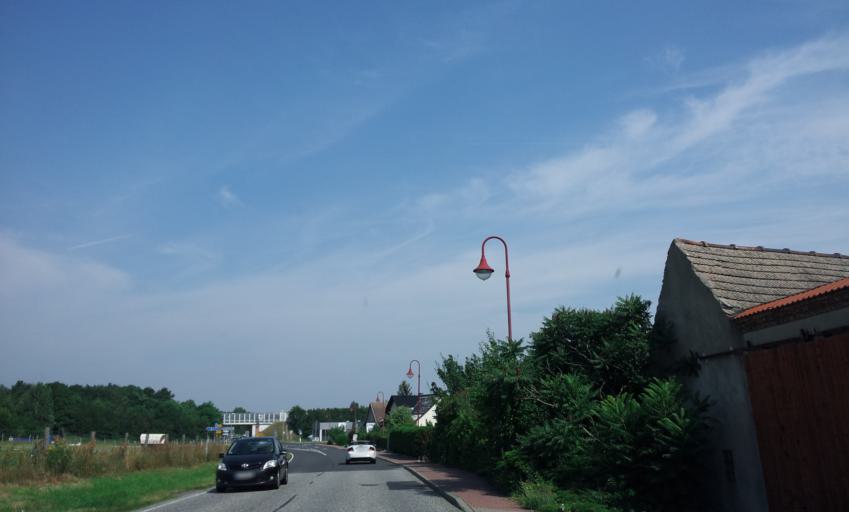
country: DE
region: Brandenburg
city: Linthe
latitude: 52.1560
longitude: 12.7849
